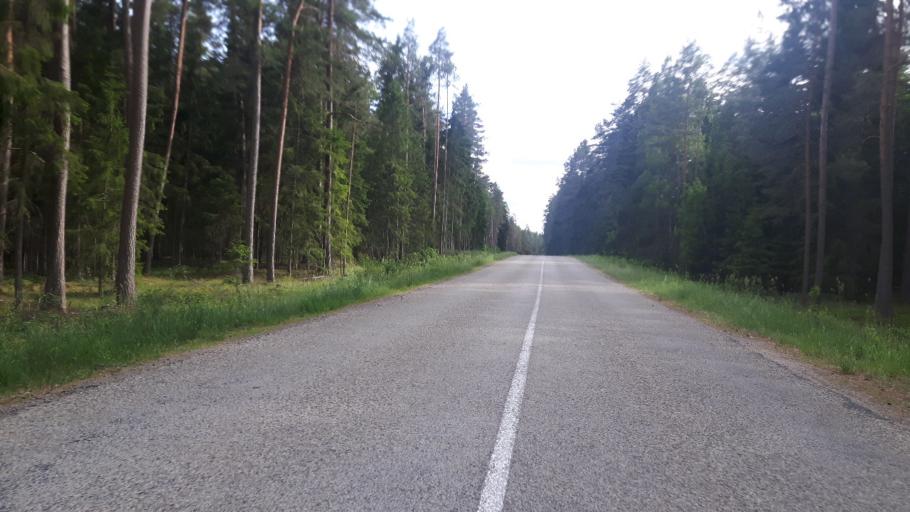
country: LV
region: Engure
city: Smarde
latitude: 57.0068
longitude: 23.3350
